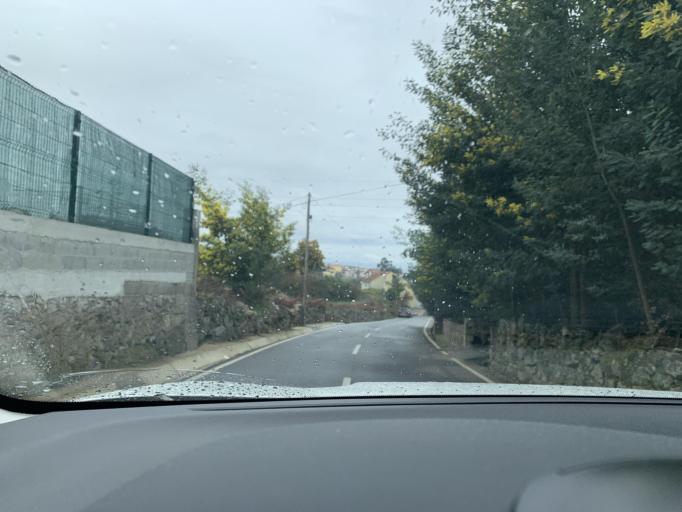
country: PT
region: Viseu
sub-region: Mangualde
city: Mangualde
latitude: 40.6020
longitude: -7.7863
